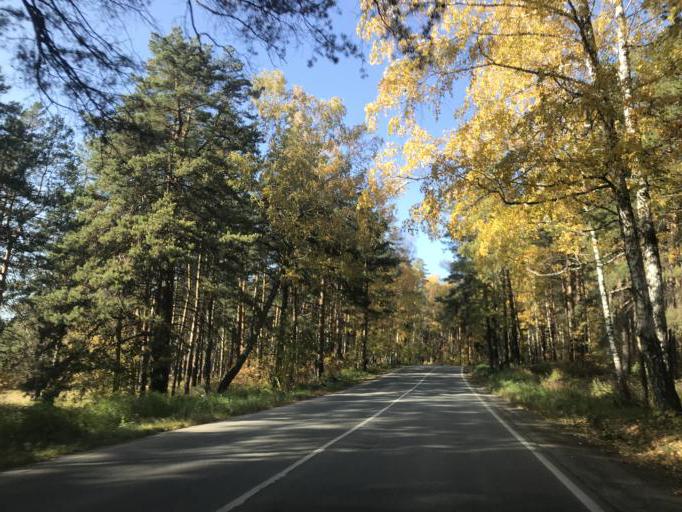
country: RU
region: Chelyabinsk
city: Dolgoderevenskoye
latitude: 55.2878
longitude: 61.3574
